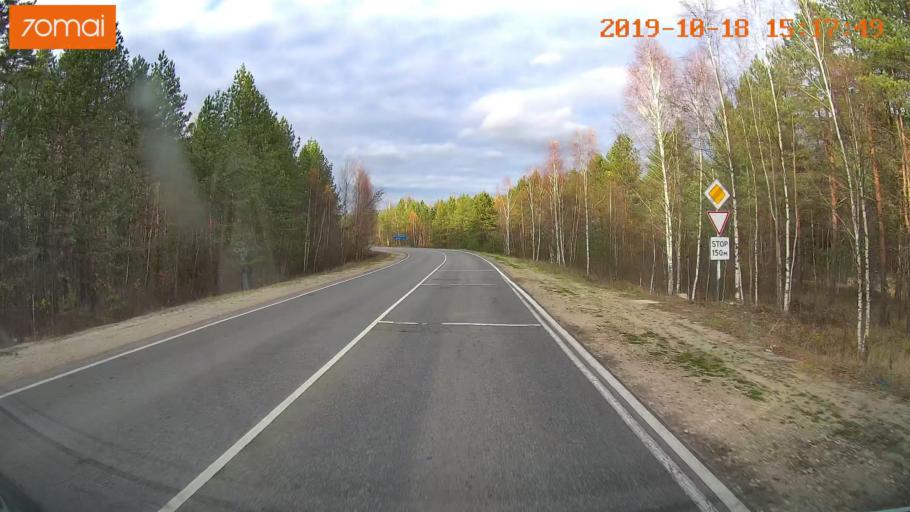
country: RU
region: Vladimir
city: Anopino
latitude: 55.6553
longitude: 40.7273
